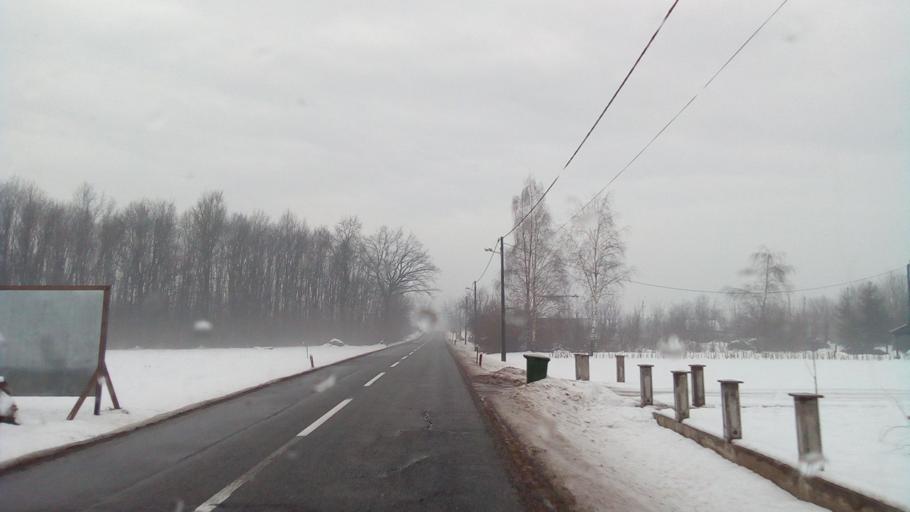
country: HR
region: Sisacko-Moslavacka
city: Petrinja
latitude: 45.4670
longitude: 16.2545
